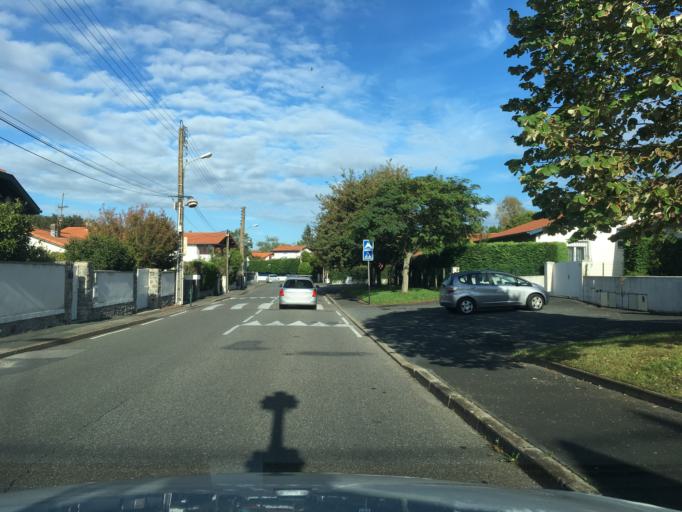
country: FR
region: Aquitaine
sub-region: Departement des Pyrenees-Atlantiques
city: Biarritz
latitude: 43.4635
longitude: -1.5569
